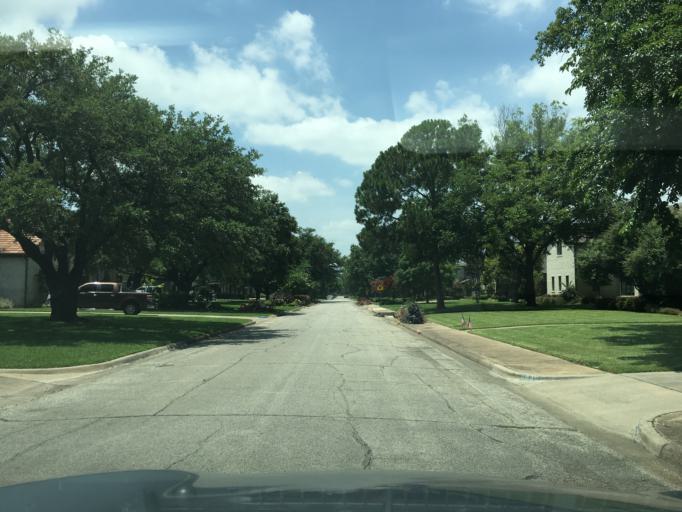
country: US
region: Texas
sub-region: Dallas County
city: Addison
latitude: 32.9175
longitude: -96.8053
